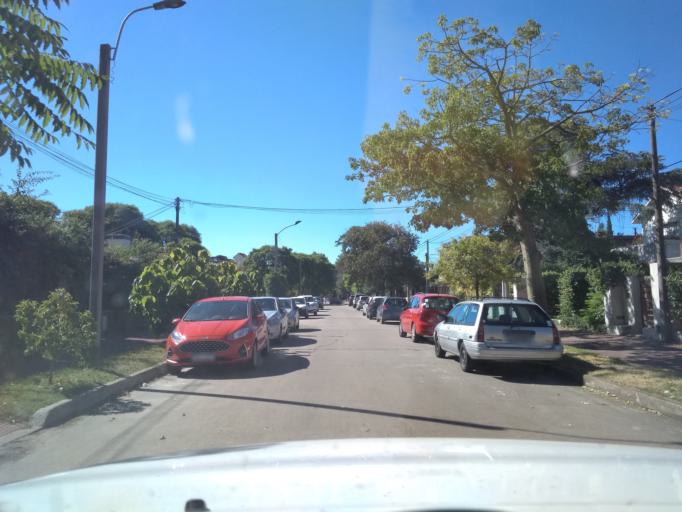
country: UY
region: Canelones
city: Paso de Carrasco
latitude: -34.8915
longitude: -56.0617
